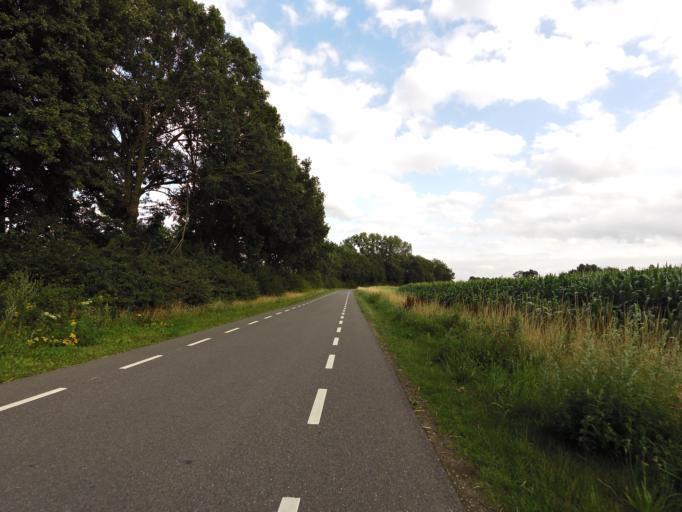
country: NL
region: Gelderland
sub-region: Gemeente Doesburg
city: Doesburg
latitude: 51.9718
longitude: 6.1603
